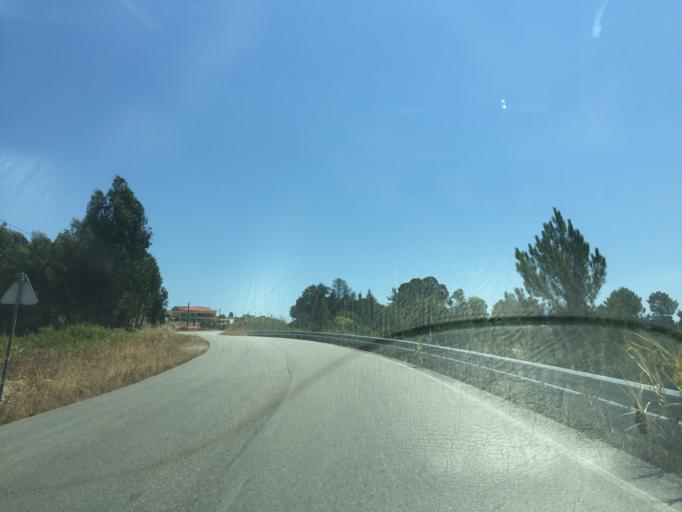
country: PT
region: Santarem
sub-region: Tomar
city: Tomar
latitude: 39.5967
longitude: -8.3332
